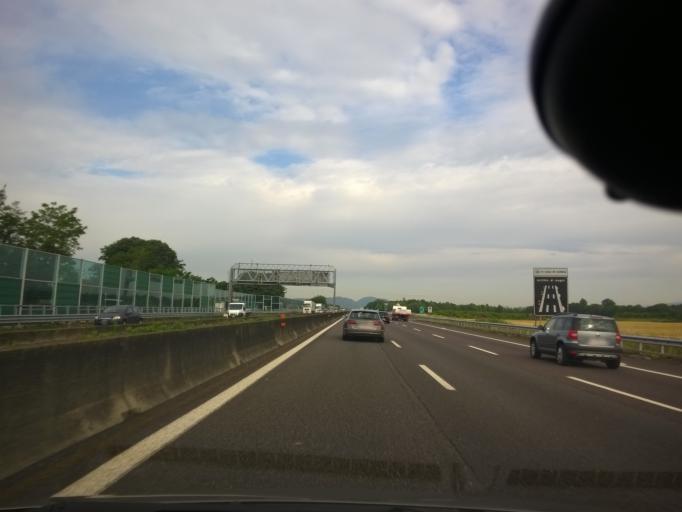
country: IT
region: Lombardy
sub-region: Provincia di Brescia
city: Ospitaletto
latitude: 45.5677
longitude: 10.0578
